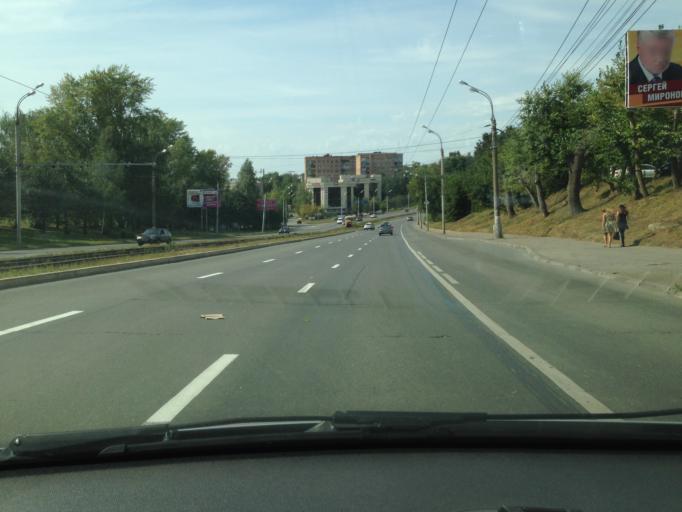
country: RU
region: Udmurtiya
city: Izhevsk
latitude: 56.8604
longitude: 53.1948
